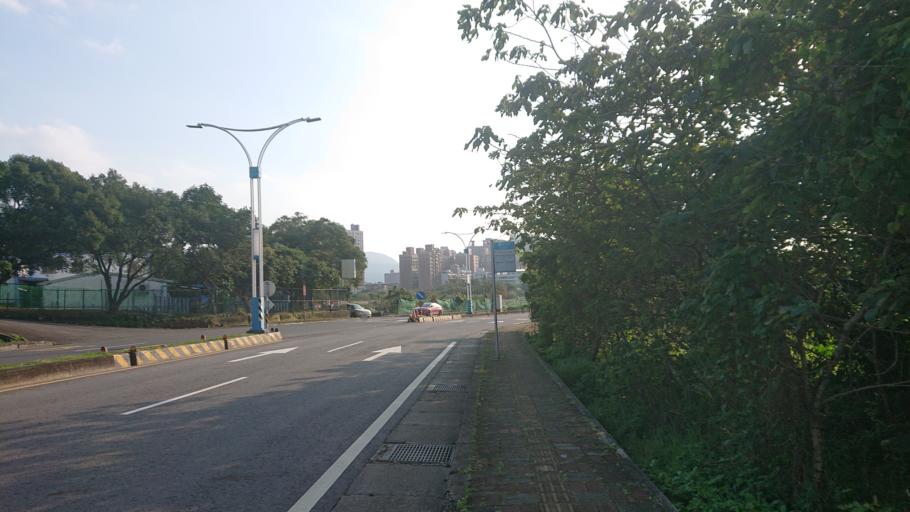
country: TW
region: Taipei
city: Taipei
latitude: 25.1891
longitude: 121.4262
